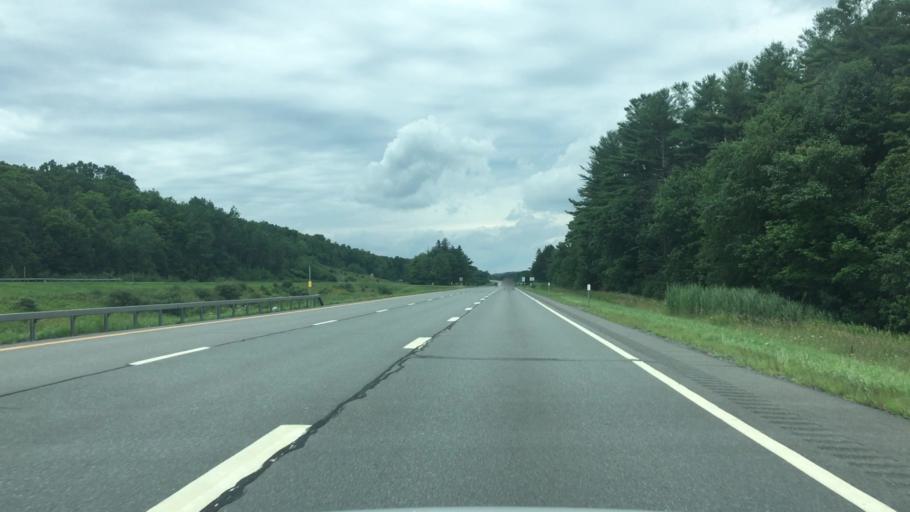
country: US
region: New York
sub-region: Albany County
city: Altamont
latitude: 42.7721
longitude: -74.0695
